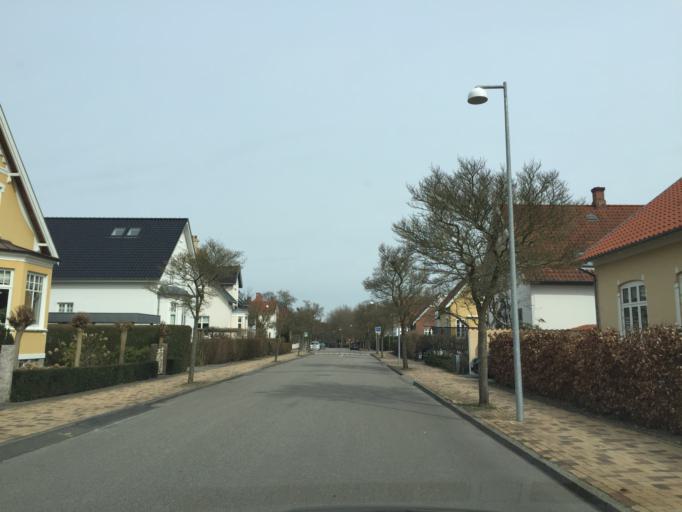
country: DK
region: South Denmark
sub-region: Odense Kommune
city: Odense
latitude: 55.3871
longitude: 10.3830
